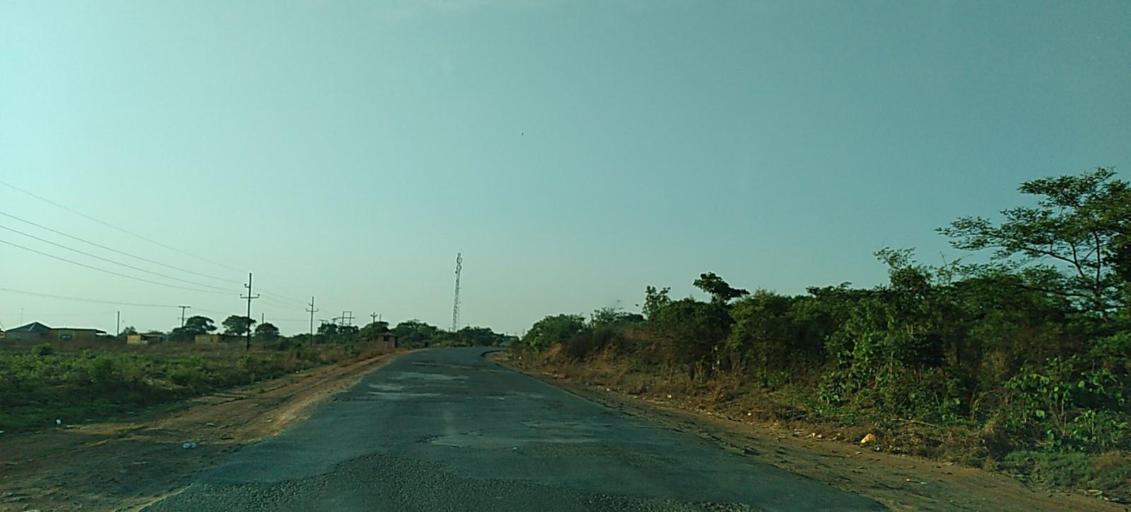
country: ZM
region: Copperbelt
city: Luanshya
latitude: -13.3067
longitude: 28.6881
